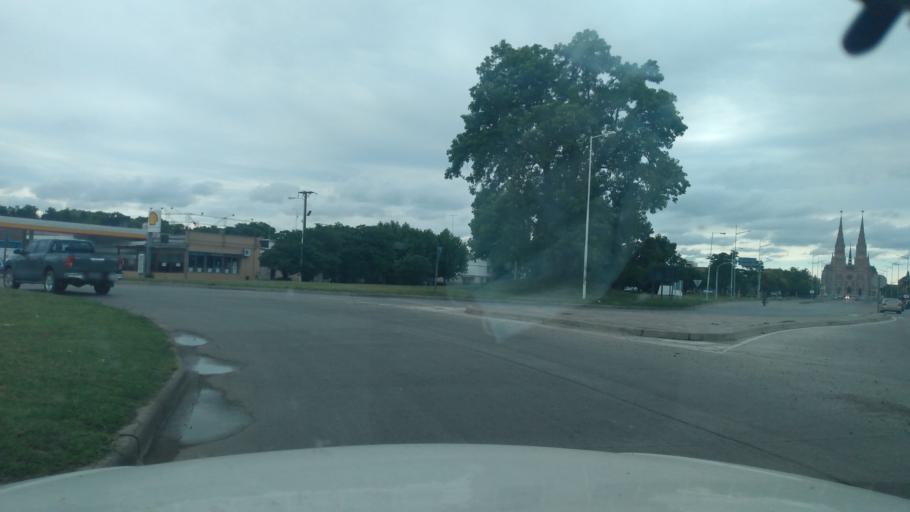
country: AR
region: Buenos Aires
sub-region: Partido de Lujan
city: Lujan
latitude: -34.5556
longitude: -59.1177
